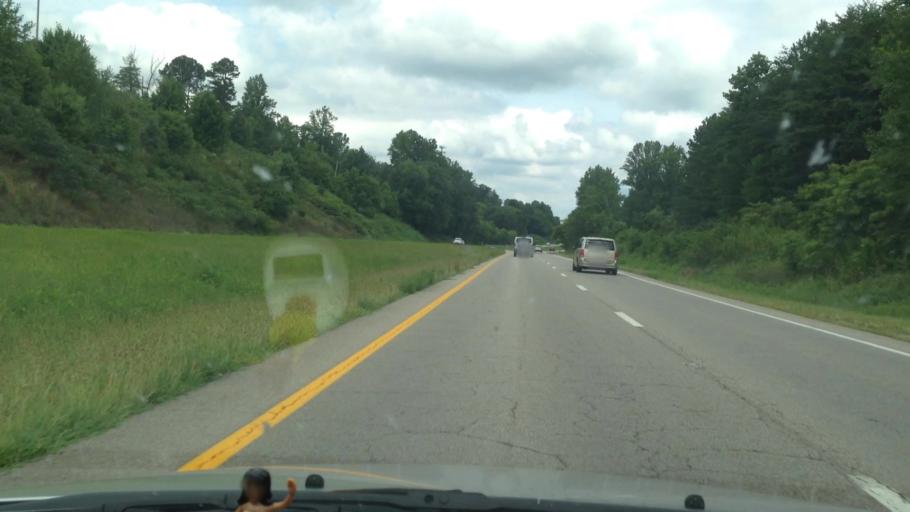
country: US
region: Virginia
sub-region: Pittsylvania County
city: Motley
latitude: 37.0135
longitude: -79.3569
